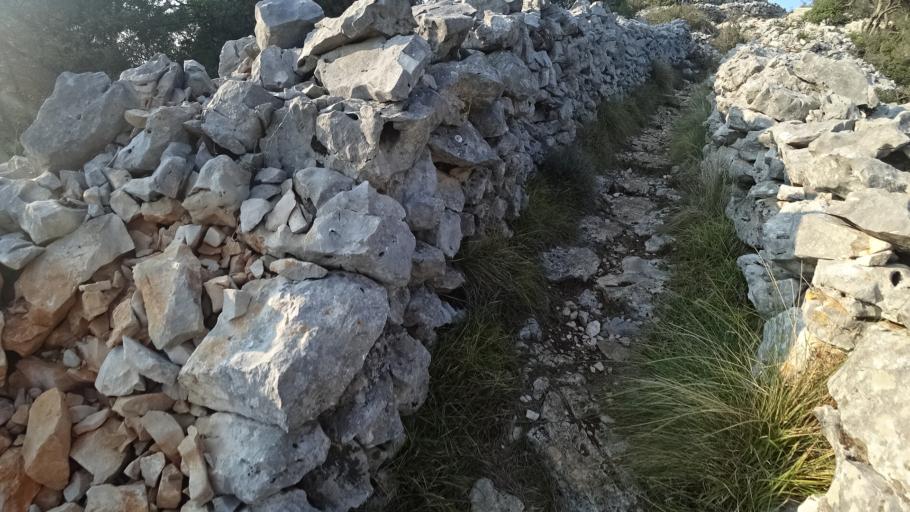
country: HR
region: Primorsko-Goranska
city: Mali Losinj
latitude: 44.5193
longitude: 14.4767
